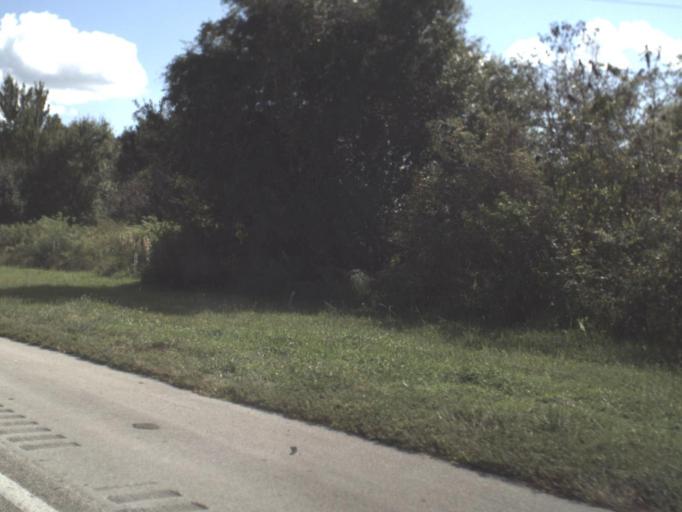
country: US
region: Florida
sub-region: Osceola County
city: Saint Cloud
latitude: 28.0626
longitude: -81.2350
